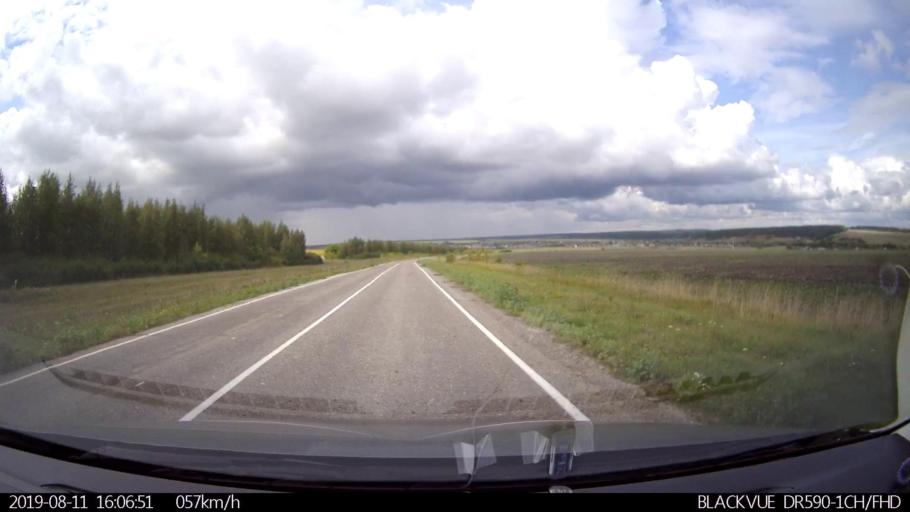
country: RU
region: Ulyanovsk
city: Ignatovka
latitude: 53.9720
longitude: 47.6471
